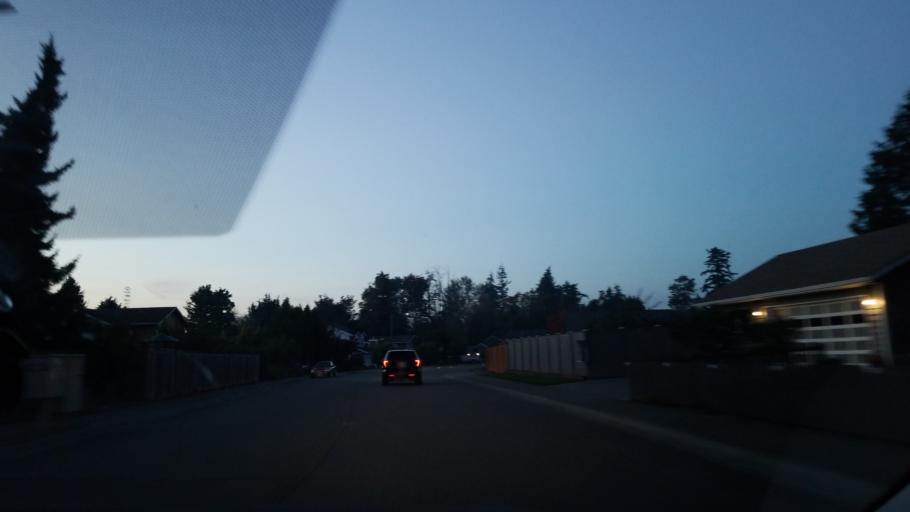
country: US
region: Washington
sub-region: Snohomish County
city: Silver Firs
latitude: 47.8787
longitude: -122.1733
